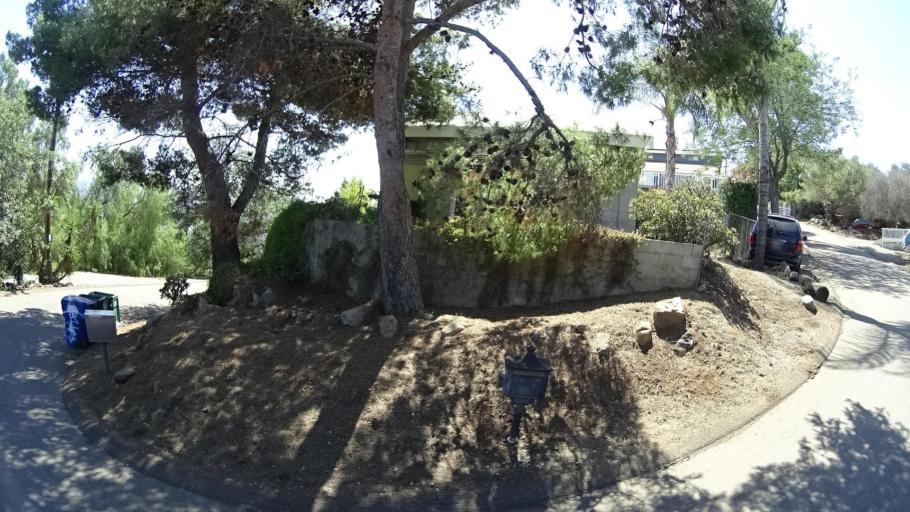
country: US
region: California
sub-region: San Diego County
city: Crest
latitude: 32.8088
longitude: -116.8608
